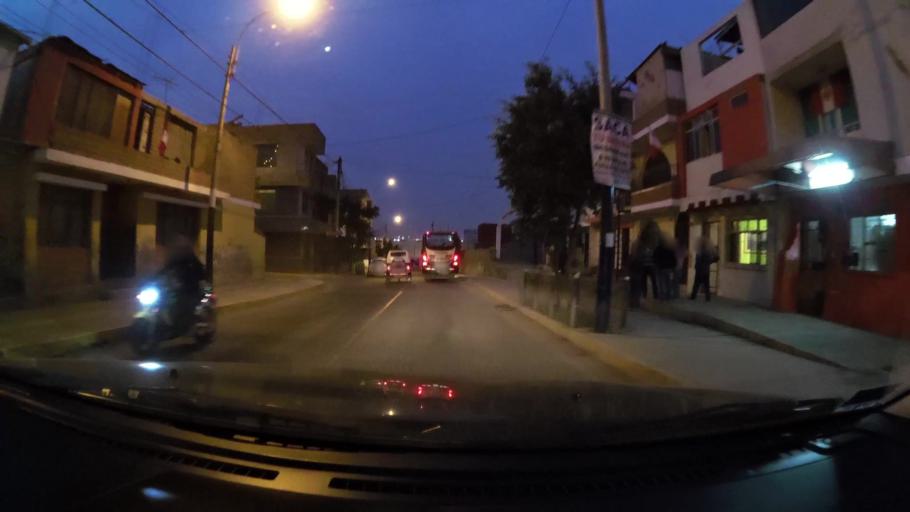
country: PE
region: Lima
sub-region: Lima
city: Surco
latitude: -12.1782
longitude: -77.0215
